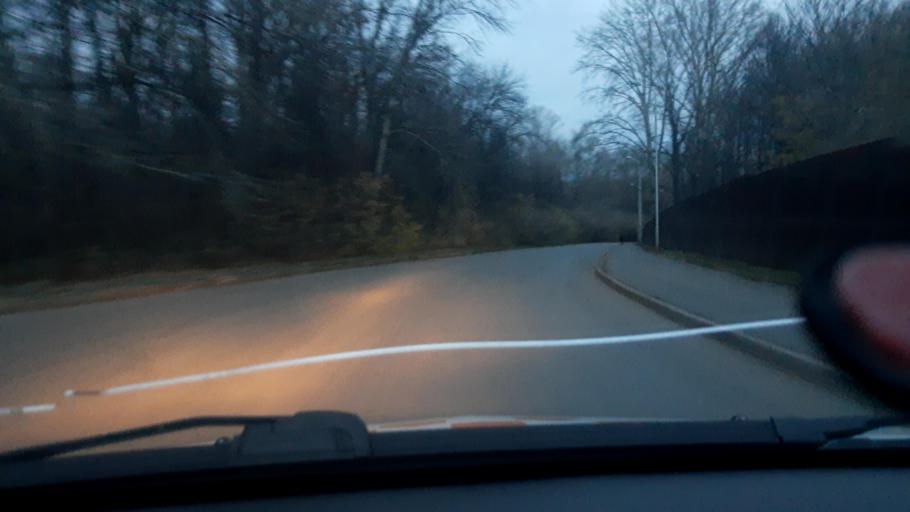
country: RU
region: Bashkortostan
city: Ufa
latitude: 54.8115
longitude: 56.0411
